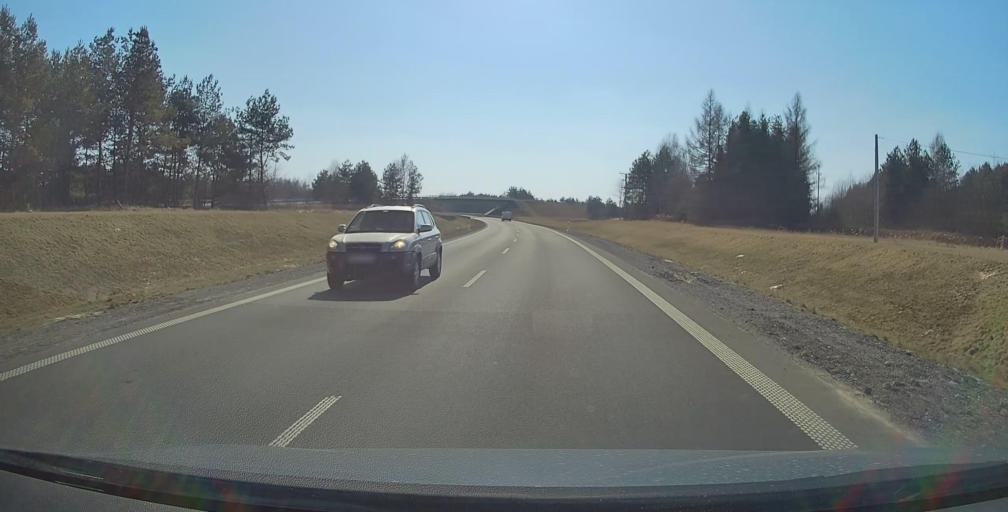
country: PL
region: Subcarpathian Voivodeship
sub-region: Powiat nizanski
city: Raclawice
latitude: 50.5030
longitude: 22.1740
